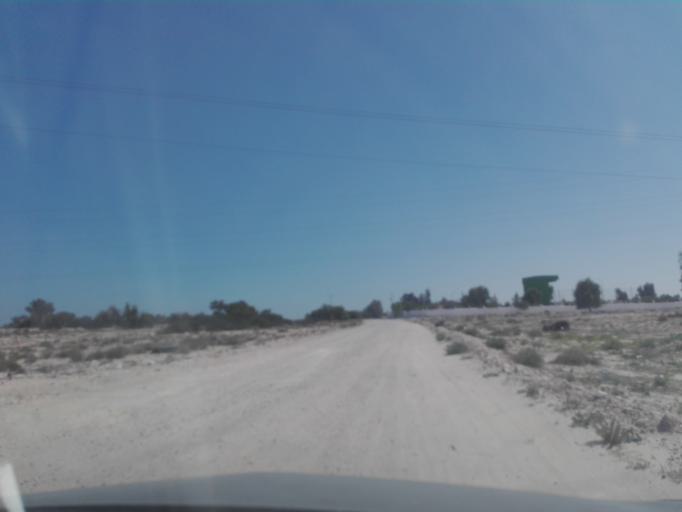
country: TN
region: Qabis
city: Gabes
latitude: 33.8732
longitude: 10.0313
